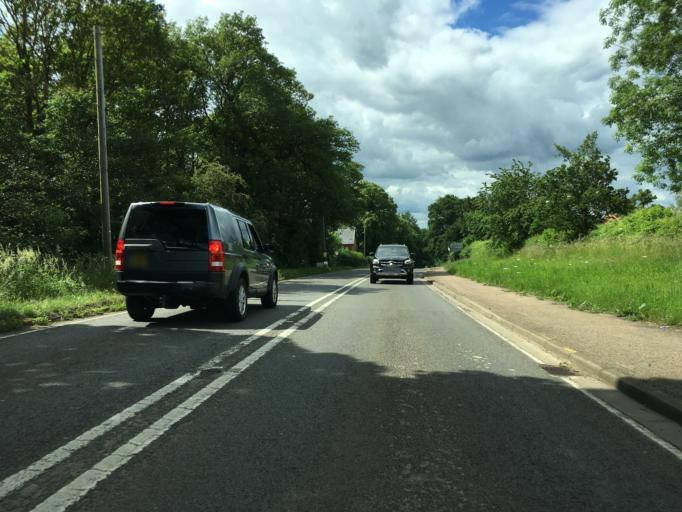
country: GB
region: England
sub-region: Oxfordshire
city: Bloxham
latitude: 52.0408
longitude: -1.3608
